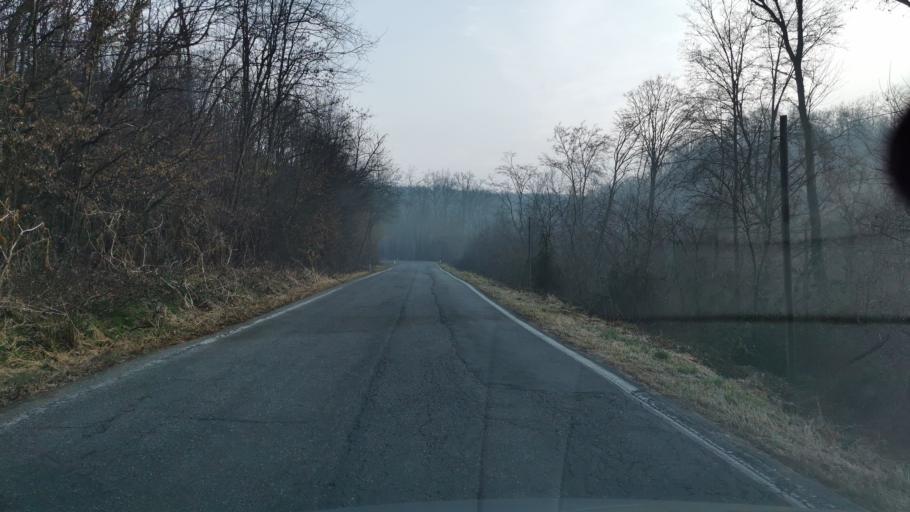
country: IT
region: Piedmont
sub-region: Provincia di Torino
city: Cuceglio
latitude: 45.3536
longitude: 7.8257
